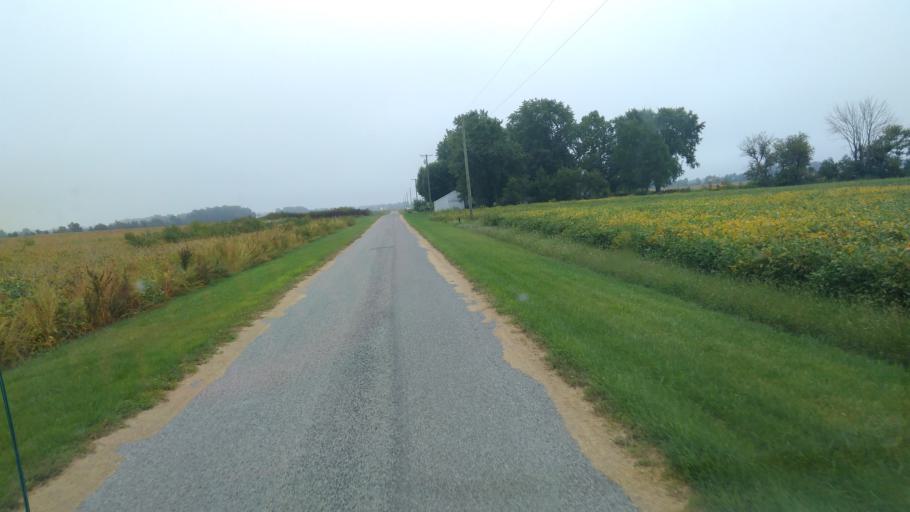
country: US
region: Ohio
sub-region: Union County
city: Richwood
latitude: 40.5003
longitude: -83.3646
